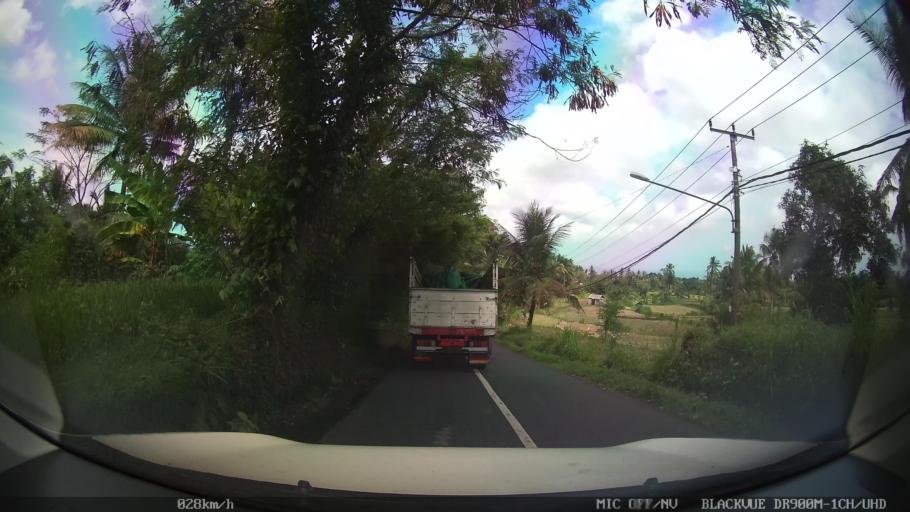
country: ID
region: Bali
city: Banjar Kelodan
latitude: -8.5138
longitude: 115.3642
